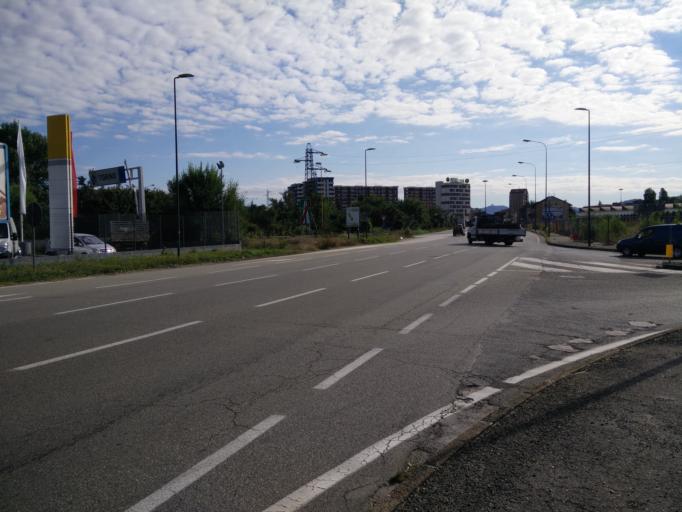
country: IT
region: Piedmont
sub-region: Provincia di Torino
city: Fornaci
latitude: 45.0299
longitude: 7.6080
